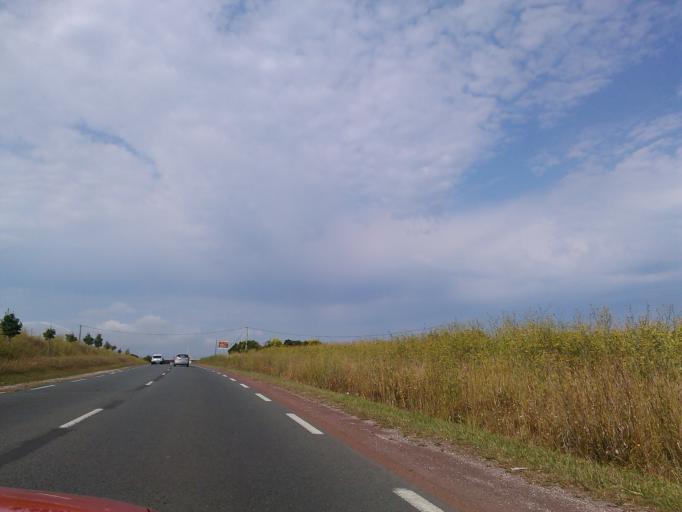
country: FR
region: Poitou-Charentes
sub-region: Departement de la Charente-Maritime
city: La Tremblade
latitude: 45.7588
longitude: -1.1332
